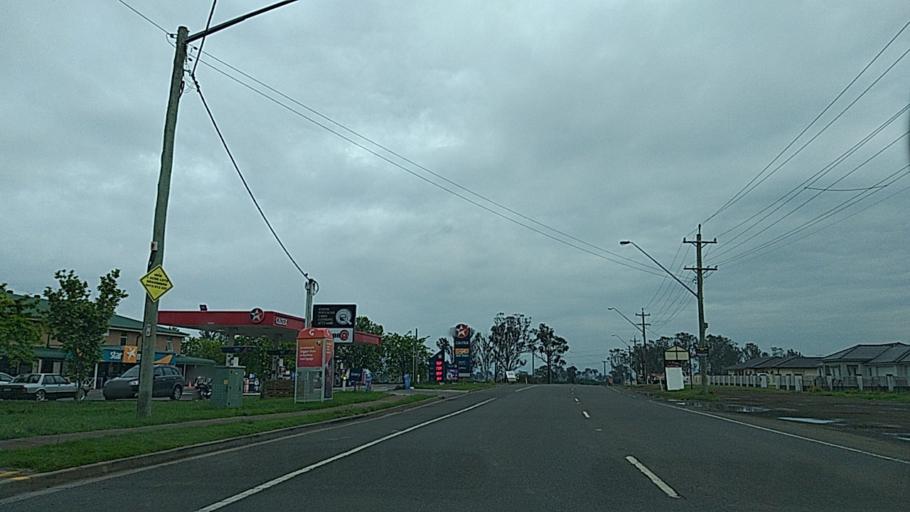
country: AU
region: New South Wales
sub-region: Liverpool
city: Luddenham
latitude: -33.8760
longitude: 150.6897
